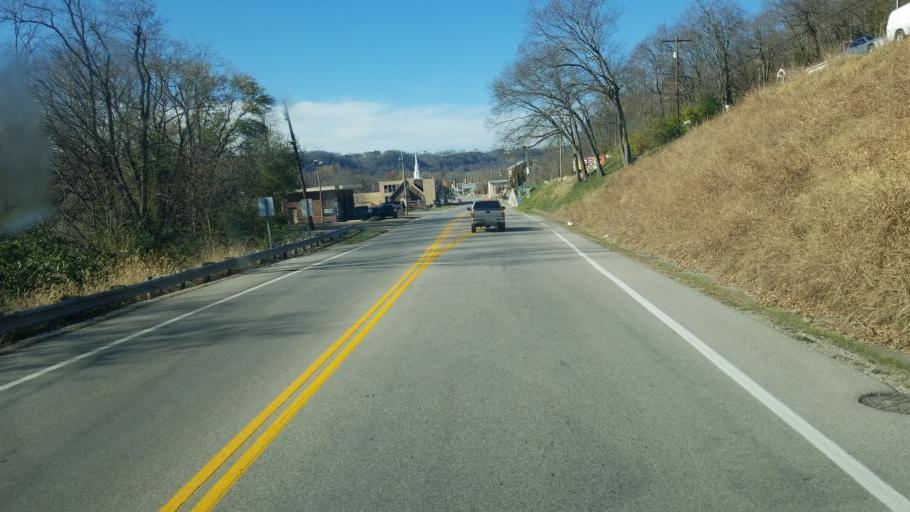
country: US
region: Ohio
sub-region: Brown County
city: Aberdeen
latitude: 38.6530
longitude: -83.7559
